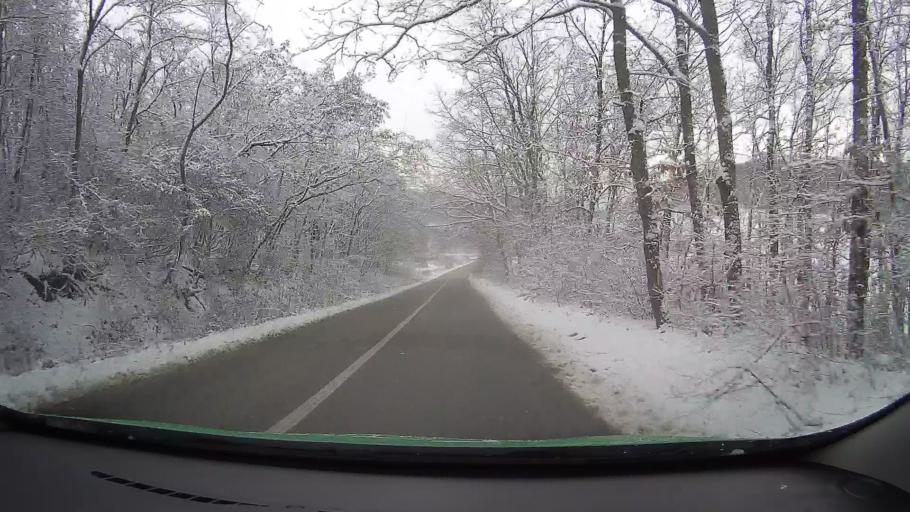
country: RO
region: Hunedoara
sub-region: Oras Hateg
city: Hateg
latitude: 45.6366
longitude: 22.9213
